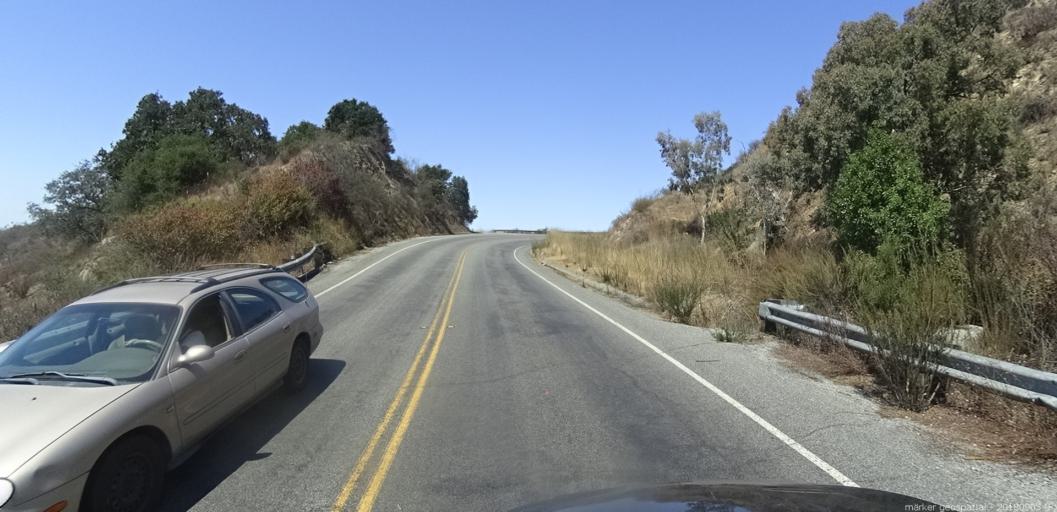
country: US
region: California
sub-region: Monterey County
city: Carmel Valley Village
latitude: 36.5199
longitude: -121.7563
